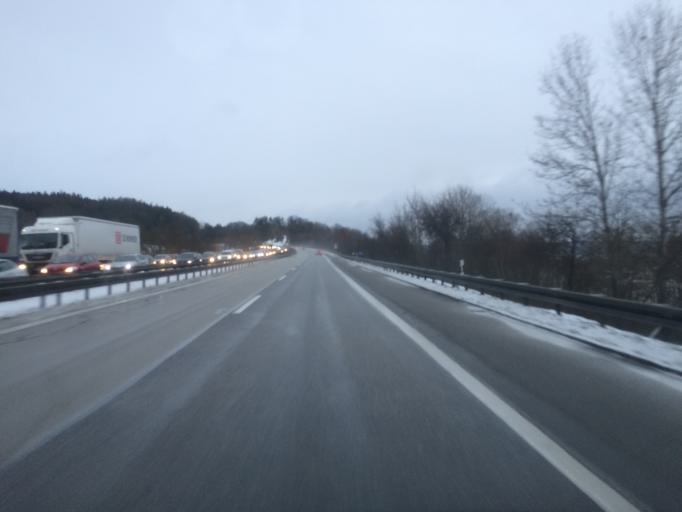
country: DE
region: Bavaria
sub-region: Upper Palatinate
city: Zeitlarn
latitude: 49.0723
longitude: 12.0961
